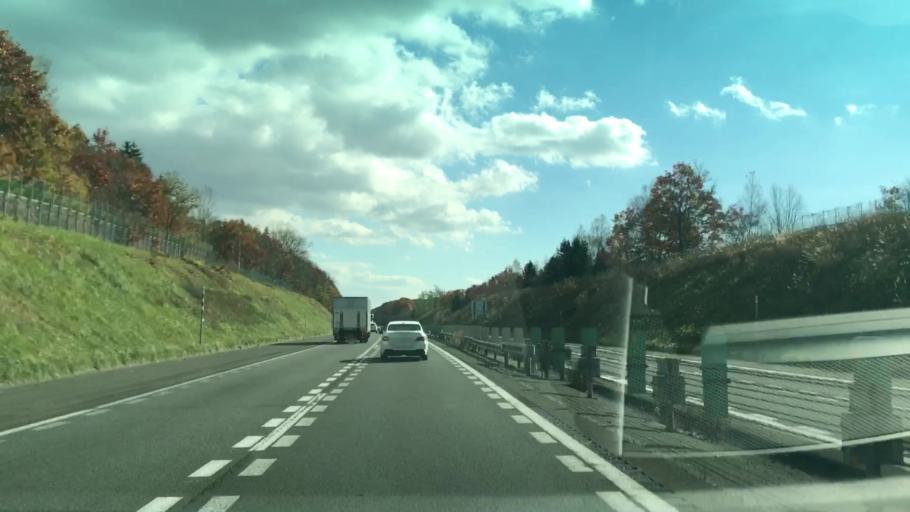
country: JP
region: Hokkaido
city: Kitahiroshima
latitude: 42.9363
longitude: 141.5254
